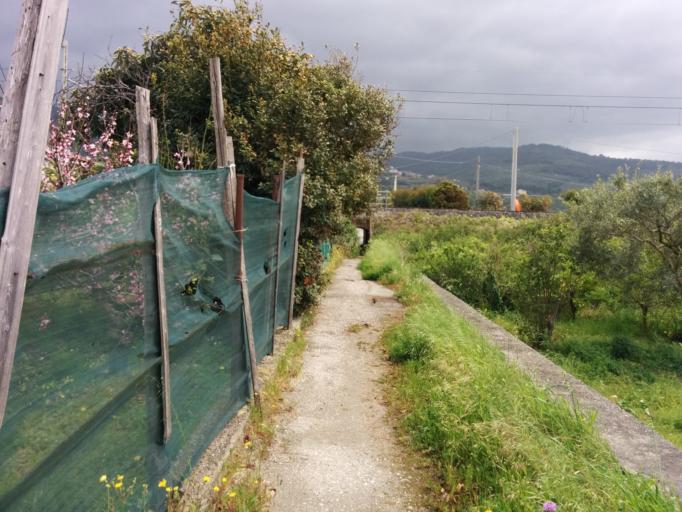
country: IT
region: Sicily
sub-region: Messina
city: Capo d'Orlando
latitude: 38.1416
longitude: 14.7252
